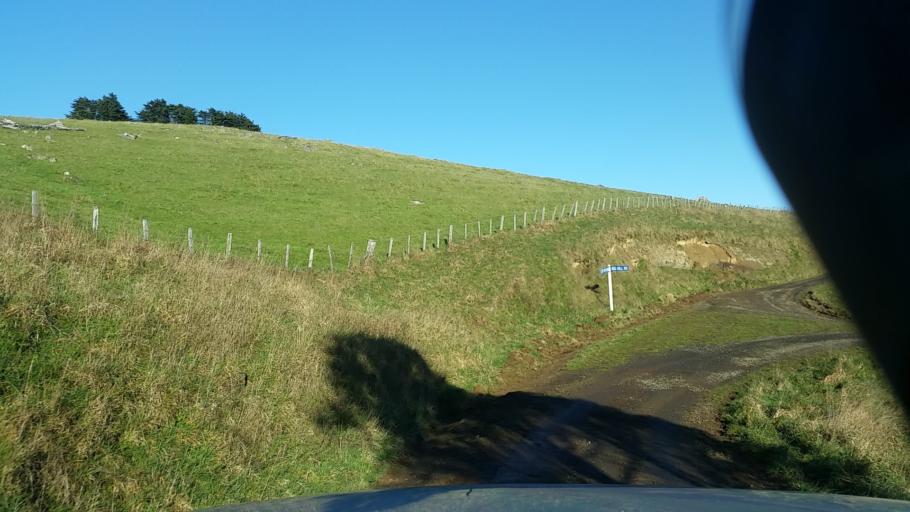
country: NZ
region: Canterbury
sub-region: Christchurch City
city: Christchurch
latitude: -43.7235
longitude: 173.0525
